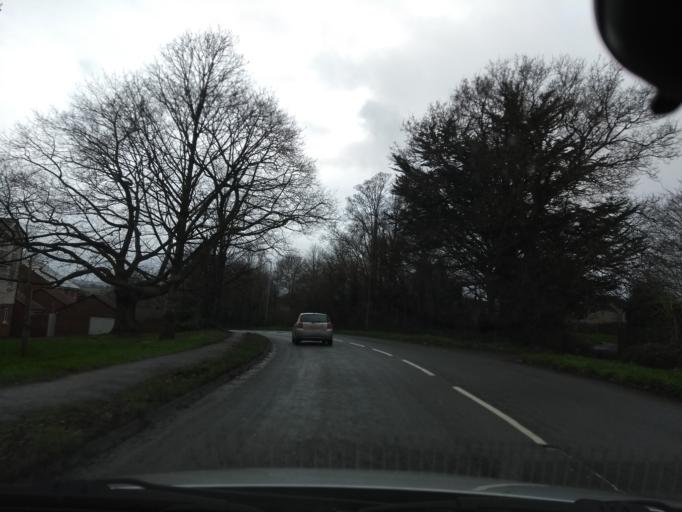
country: GB
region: England
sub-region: Somerset
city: Taunton
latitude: 51.0291
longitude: -3.1401
